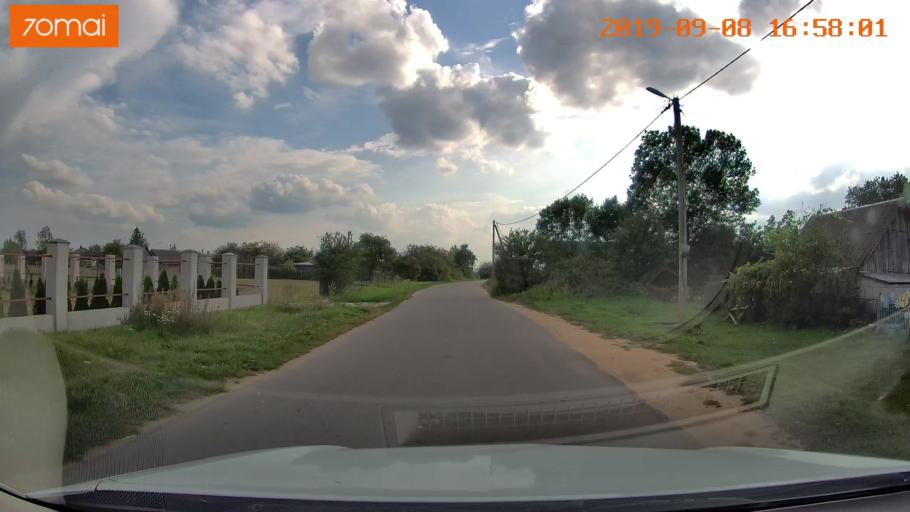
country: BY
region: Grodnenskaya
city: Hrodna
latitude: 53.7286
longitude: 23.9266
